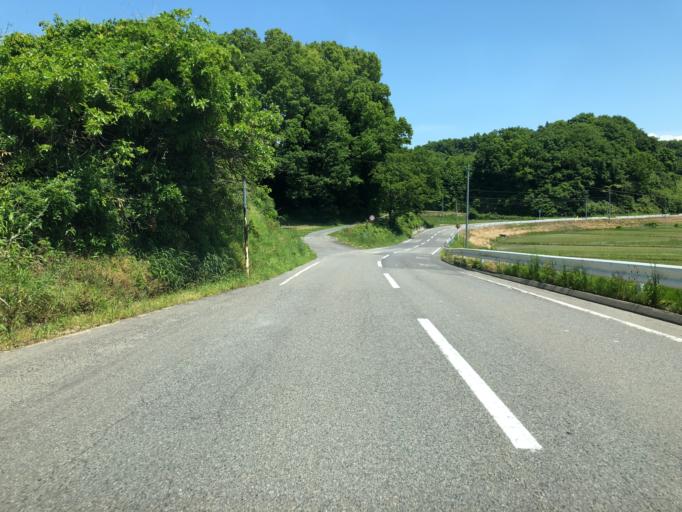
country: JP
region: Fukushima
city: Miharu
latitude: 37.4996
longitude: 140.4808
